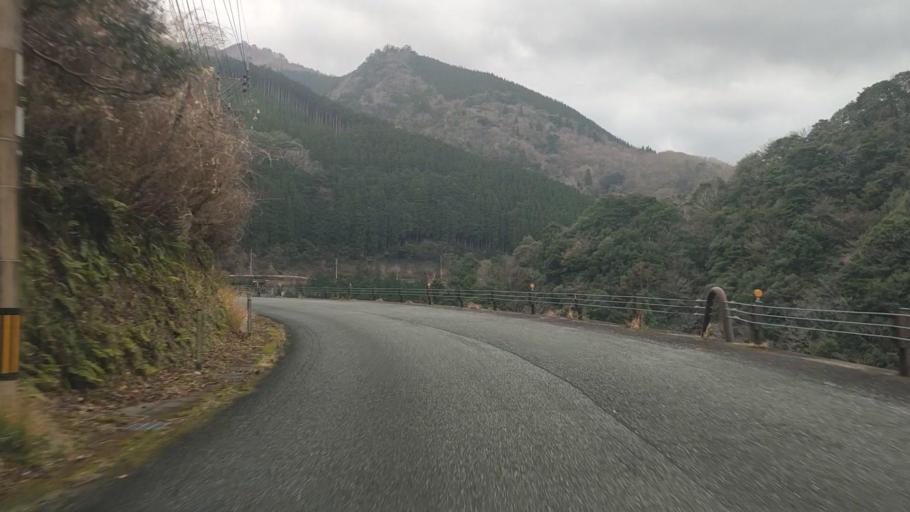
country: JP
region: Kumamoto
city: Matsubase
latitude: 32.5017
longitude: 130.9155
